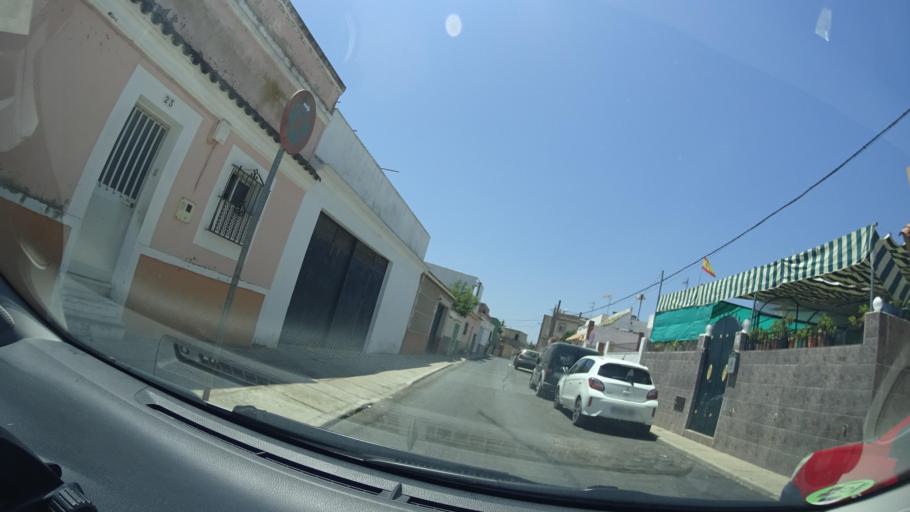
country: ES
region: Andalusia
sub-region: Provincia de Cadiz
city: Jerez de la Frontera
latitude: 36.6600
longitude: -6.1020
